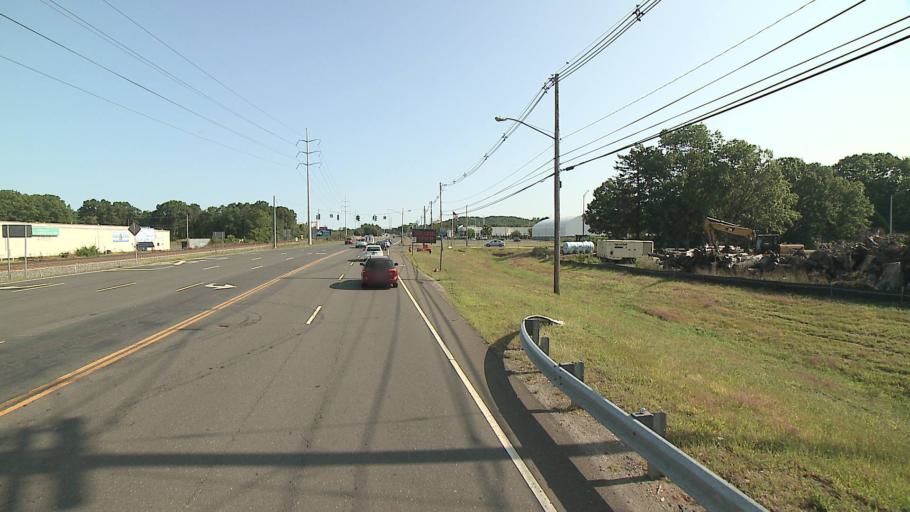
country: US
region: Connecticut
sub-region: New Haven County
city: Wallingford Center
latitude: 41.4288
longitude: -72.8371
